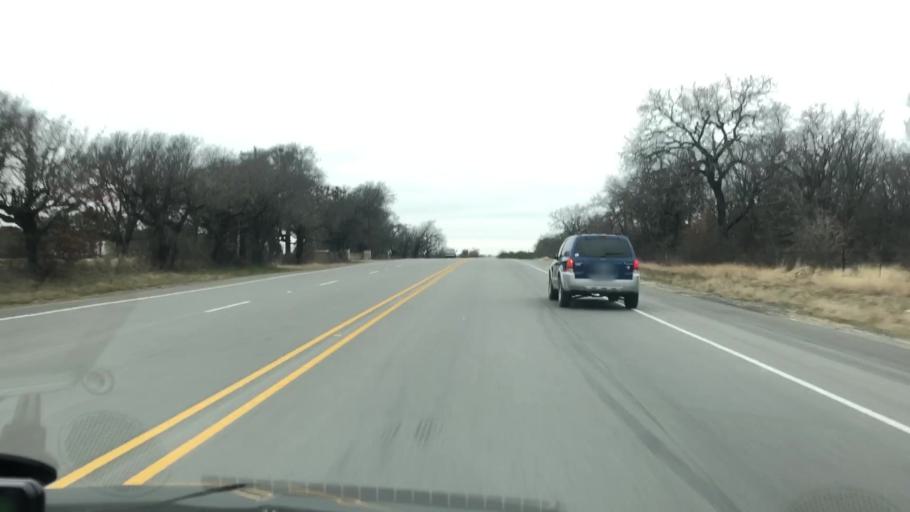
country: US
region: Texas
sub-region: Hamilton County
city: Hico
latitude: 32.0131
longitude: -98.0638
